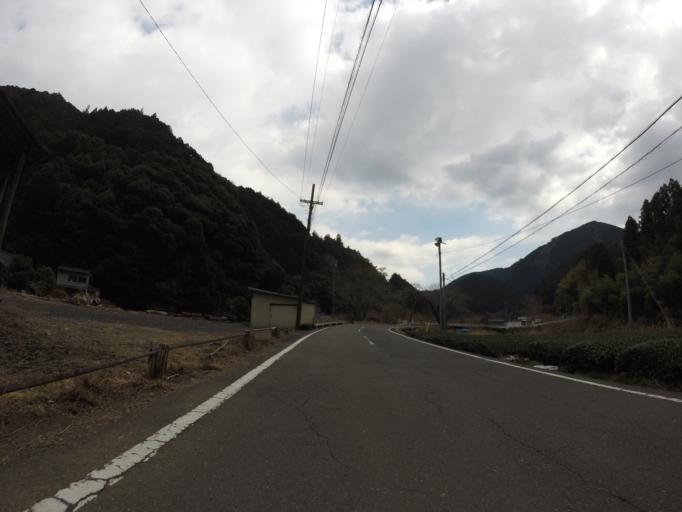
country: JP
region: Shizuoka
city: Shizuoka-shi
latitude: 35.0688
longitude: 138.3210
